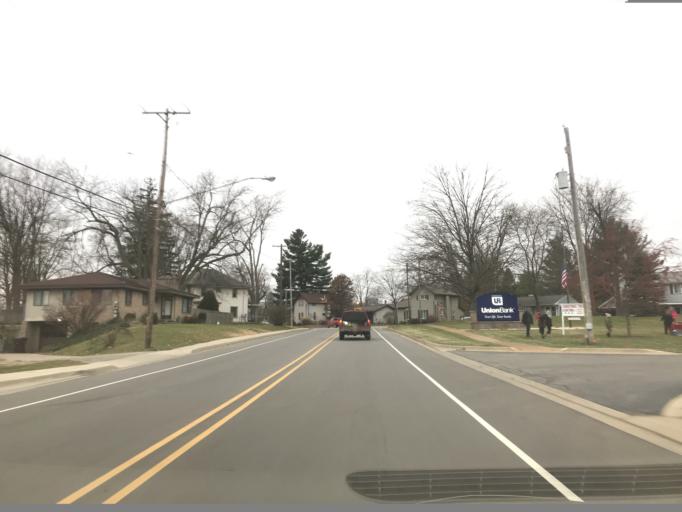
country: US
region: Michigan
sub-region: Eaton County
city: Dimondale
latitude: 42.6474
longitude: -84.6455
